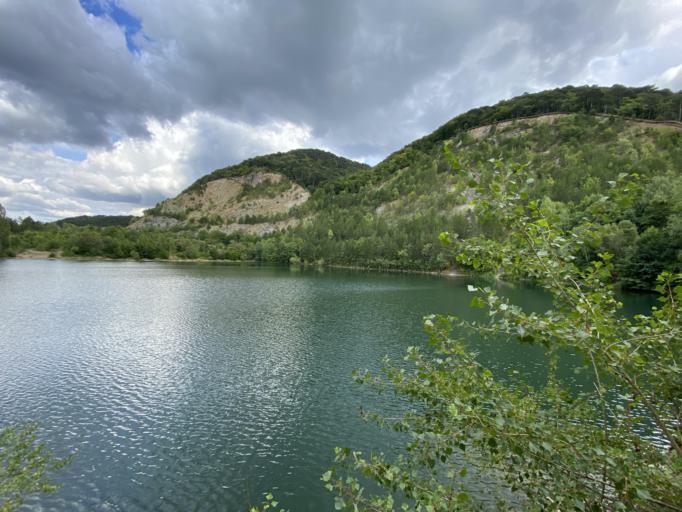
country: AT
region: Lower Austria
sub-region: Politischer Bezirk Modling
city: Kaltenleutgeben
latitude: 48.1207
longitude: 16.2210
